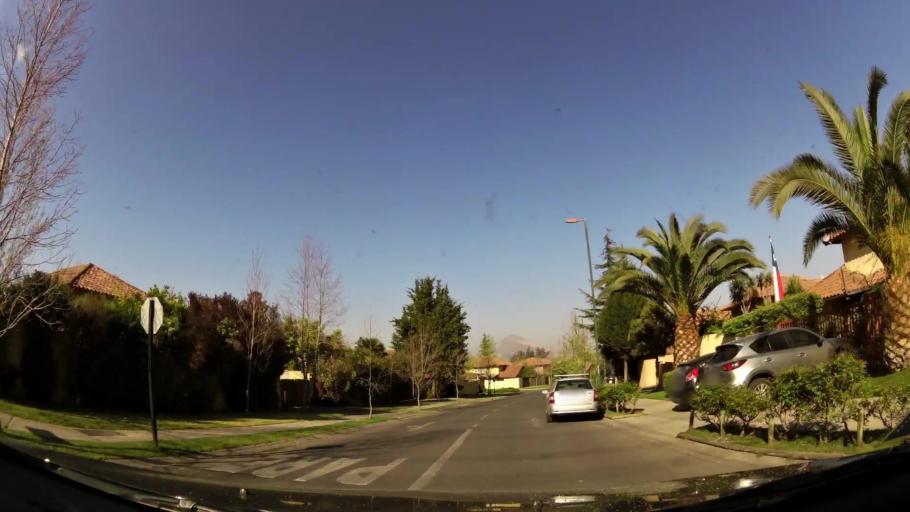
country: CL
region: Santiago Metropolitan
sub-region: Provincia de Chacabuco
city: Chicureo Abajo
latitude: -33.3487
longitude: -70.6672
